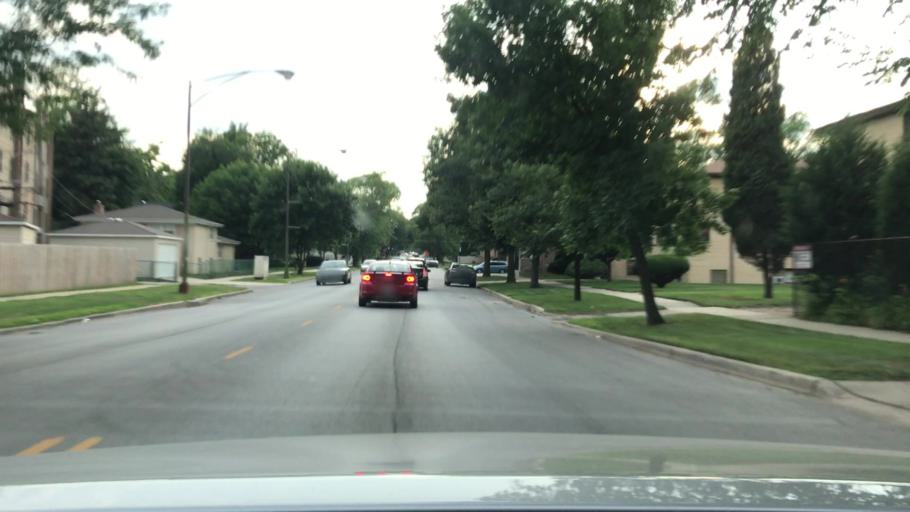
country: US
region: Illinois
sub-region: Cook County
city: Evergreen Park
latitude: 41.7140
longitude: -87.6604
